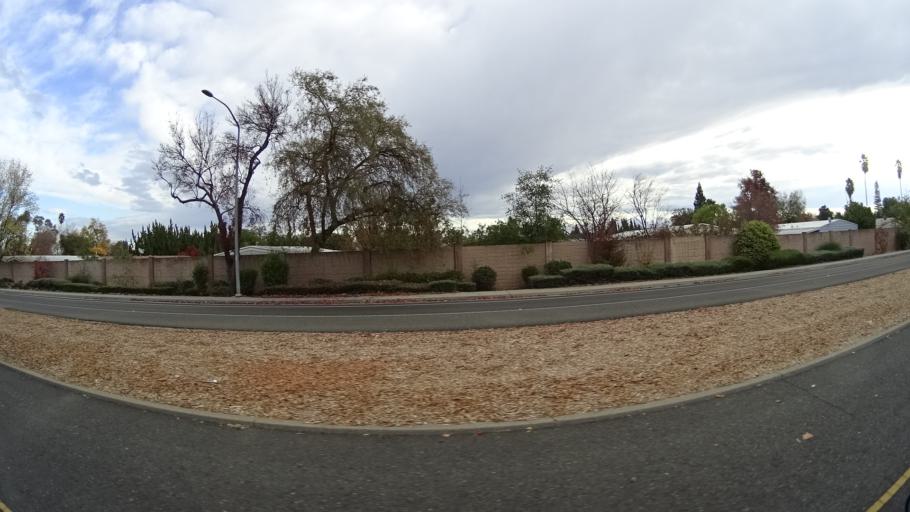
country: US
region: California
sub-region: Sacramento County
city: Citrus Heights
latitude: 38.7248
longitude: -121.2478
